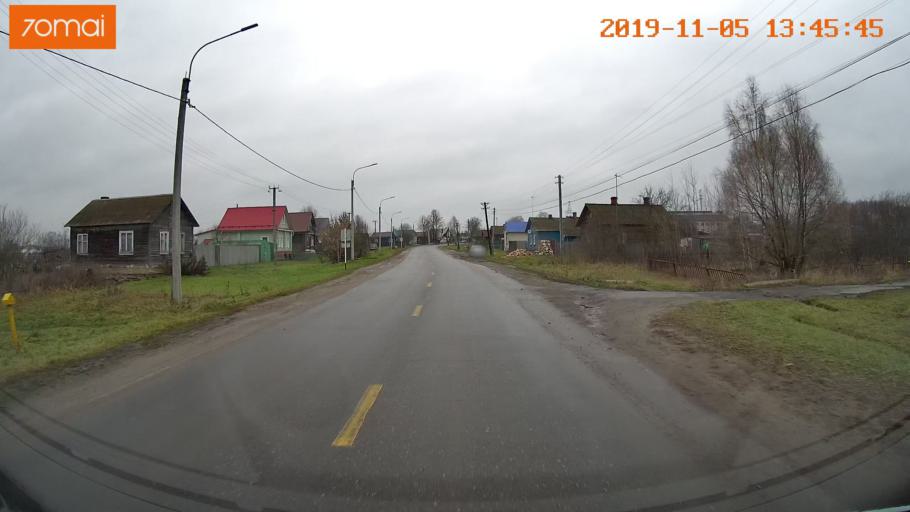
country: RU
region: Ivanovo
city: Shuya
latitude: 56.9911
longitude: 41.4117
